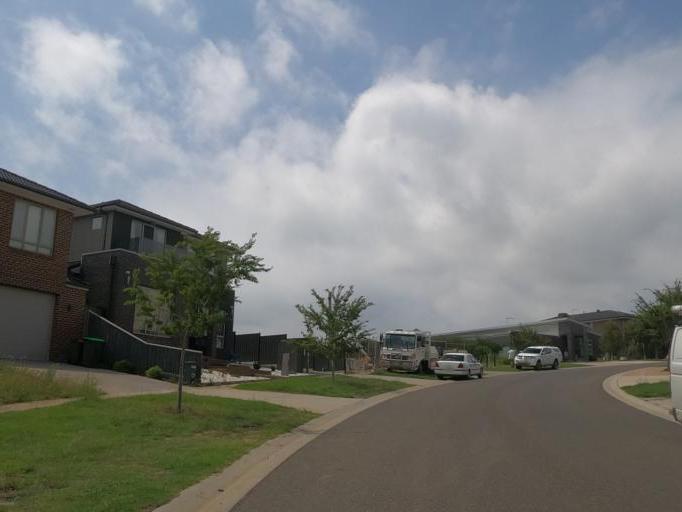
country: AU
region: Victoria
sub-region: Hume
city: Attwood
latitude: -37.6702
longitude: 144.8778
